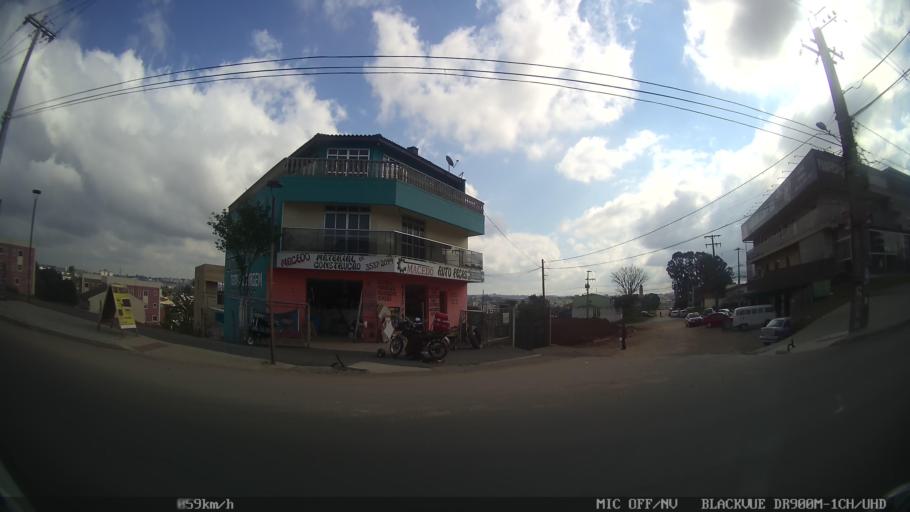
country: BR
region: Parana
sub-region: Pinhais
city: Pinhais
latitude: -25.3714
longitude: -49.1865
